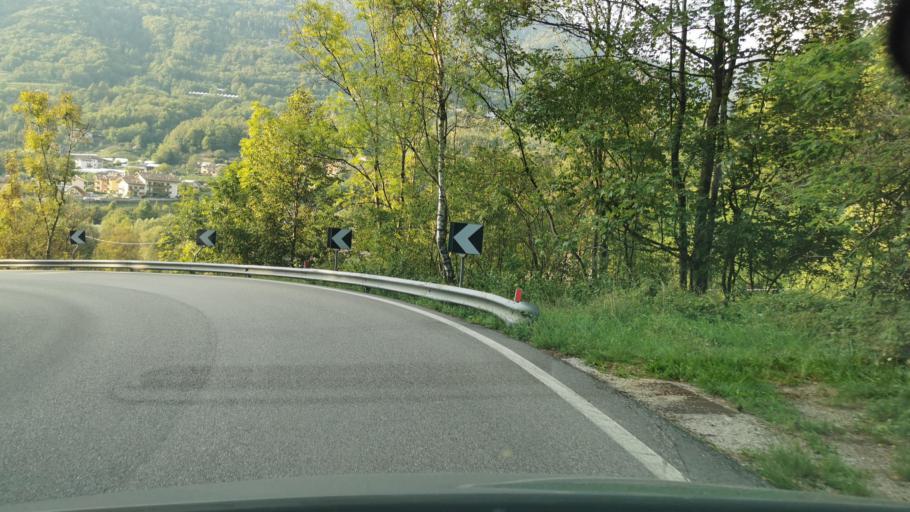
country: IT
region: Trentino-Alto Adige
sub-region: Provincia di Trento
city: Frassilongo
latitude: 46.0771
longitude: 11.2819
